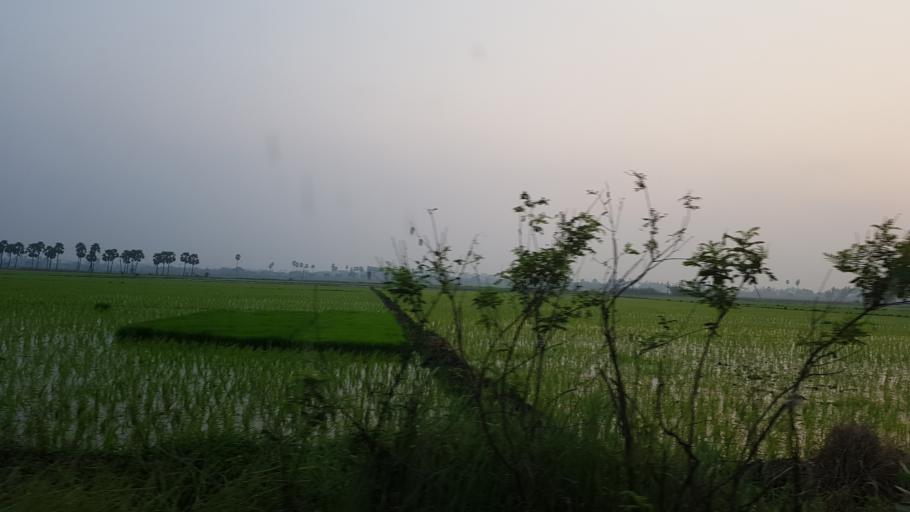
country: IN
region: Andhra Pradesh
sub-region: Krishna
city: Kankipadu
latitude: 16.4574
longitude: 80.7659
